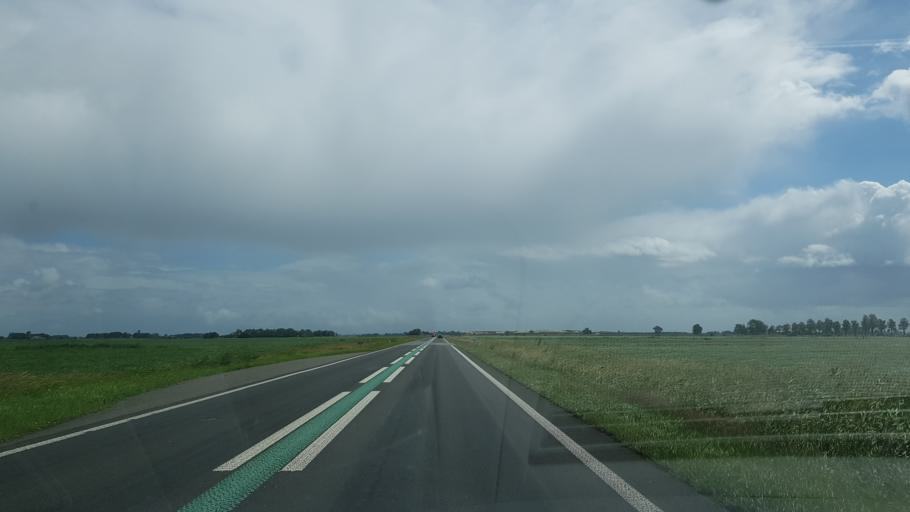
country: NL
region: Friesland
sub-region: Gemeente Ferwerderadiel
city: Burdaard
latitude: 53.2742
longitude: 5.8880
